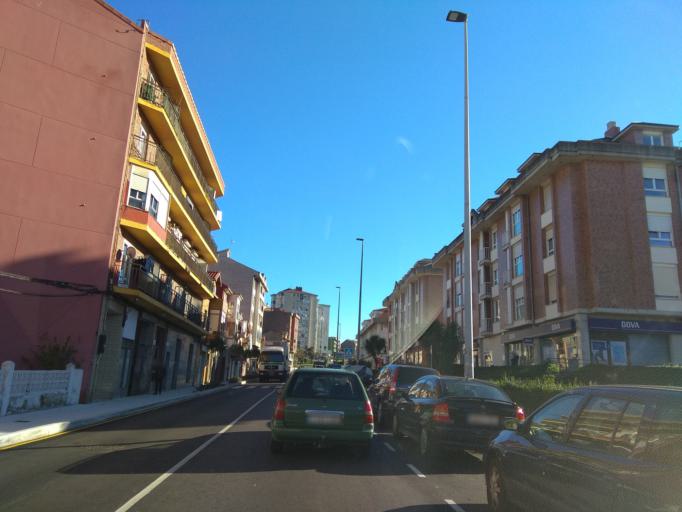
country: ES
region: Cantabria
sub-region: Provincia de Cantabria
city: Santander
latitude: 43.4623
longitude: -3.8369
